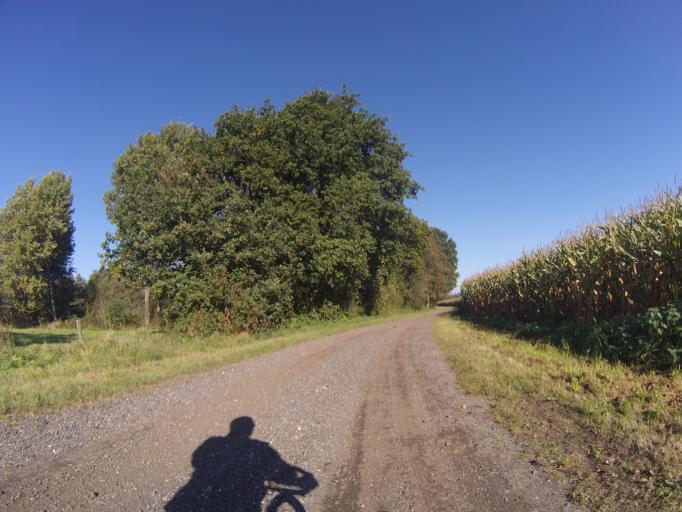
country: NL
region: Drenthe
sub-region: Gemeente Coevorden
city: Dalen
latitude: 52.7379
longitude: 6.6580
